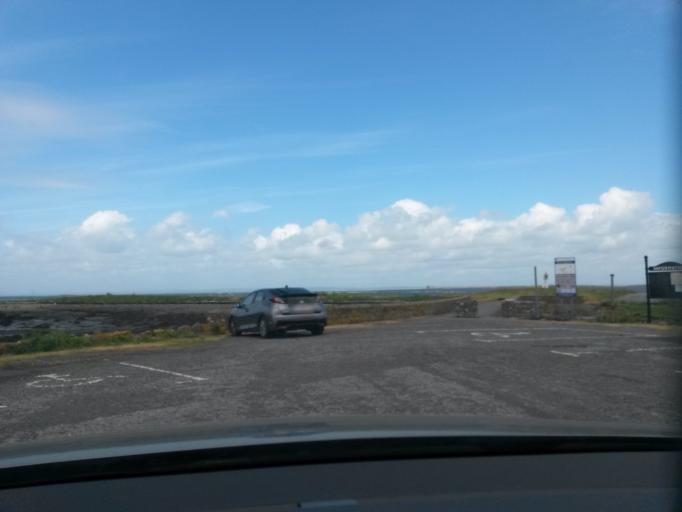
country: IE
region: Connaught
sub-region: County Galway
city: Bearna
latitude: 53.1297
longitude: -9.1291
